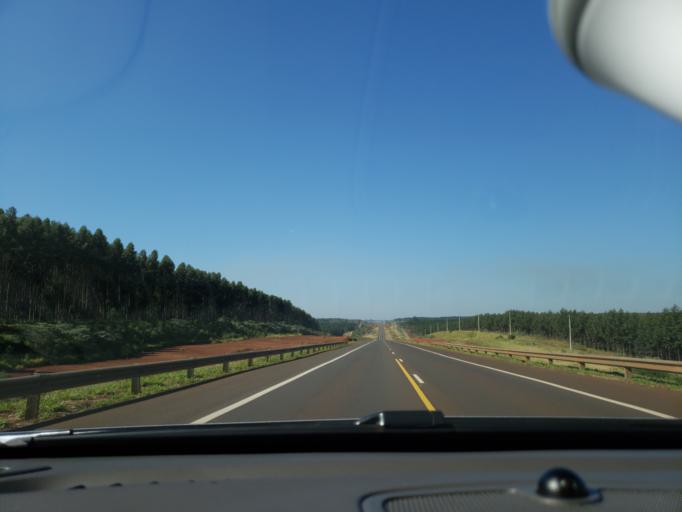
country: AR
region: Misiones
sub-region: Departamento de Capital
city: Posadas
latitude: -27.4654
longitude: -55.9419
